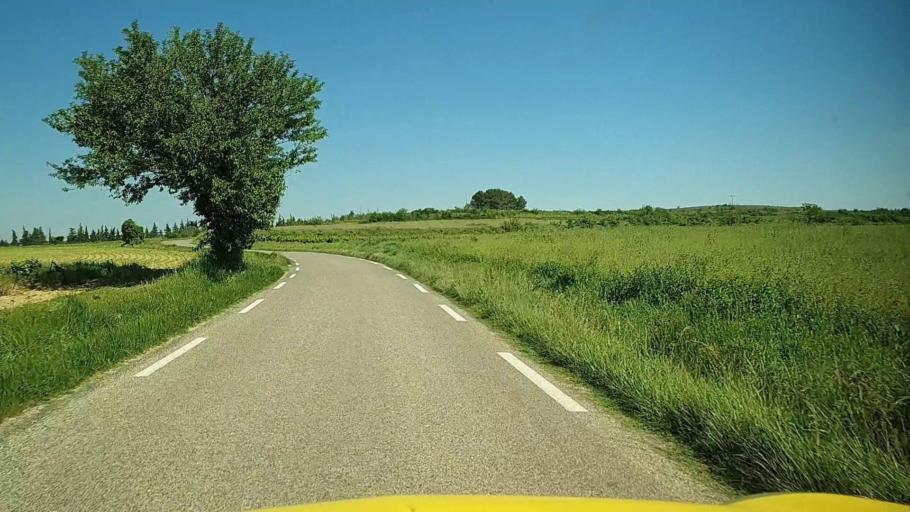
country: FR
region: Languedoc-Roussillon
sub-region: Departement du Gard
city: Saint-Chaptes
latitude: 43.9489
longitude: 4.3072
